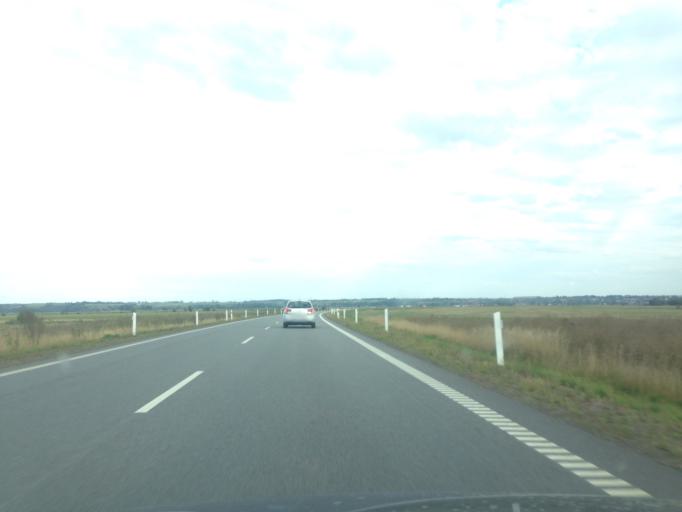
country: PL
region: Pomeranian Voivodeship
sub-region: Powiat kwidzynski
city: Kwidzyn
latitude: 53.7614
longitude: 18.8649
